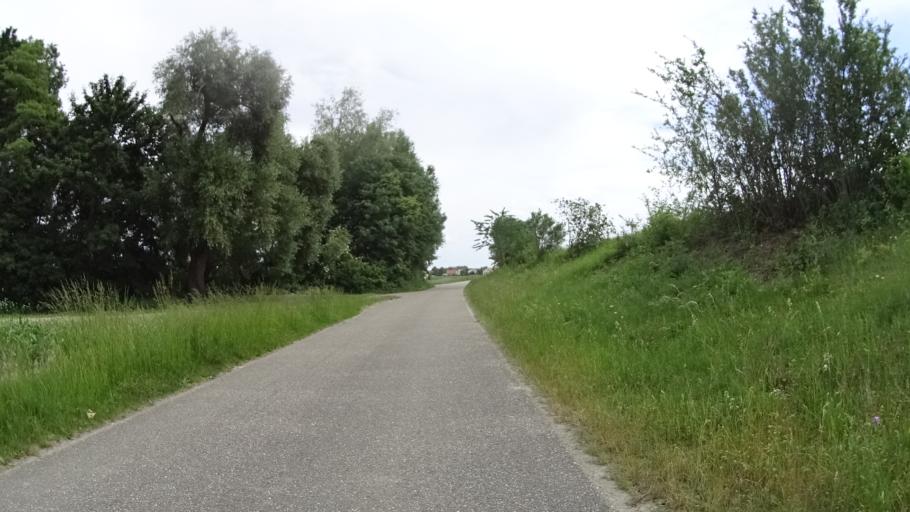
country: DE
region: Bavaria
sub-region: Upper Palatinate
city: Donaustauf
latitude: 49.0193
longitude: 12.2610
